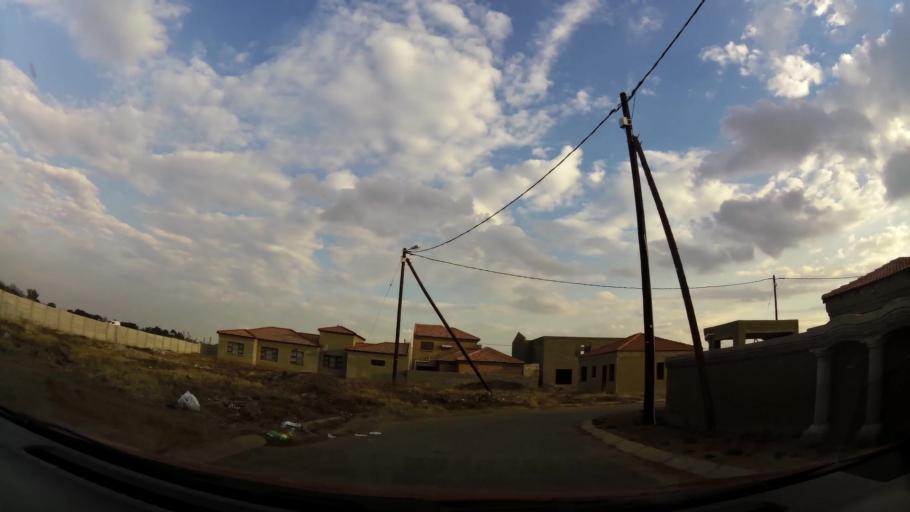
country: ZA
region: Gauteng
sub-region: Sedibeng District Municipality
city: Vanderbijlpark
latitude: -26.6104
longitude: 27.8145
